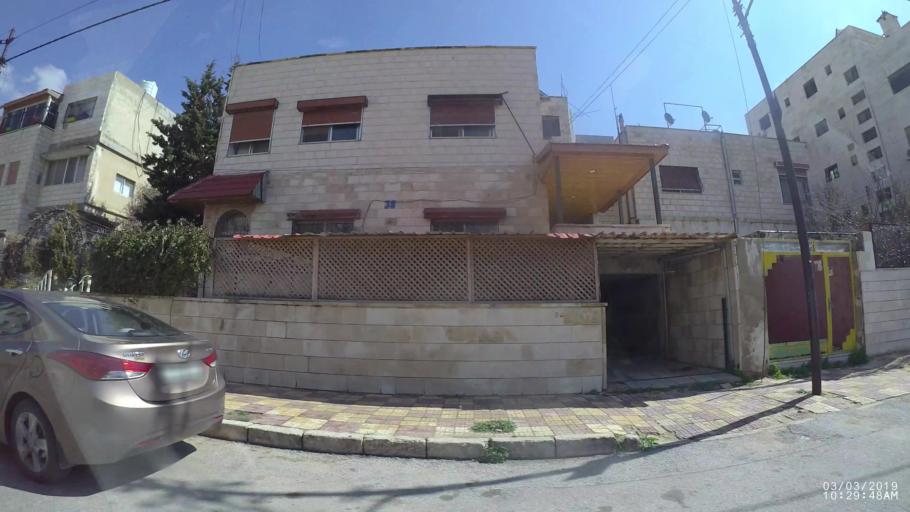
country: JO
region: Amman
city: Al Jubayhah
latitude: 31.9934
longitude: 35.9051
